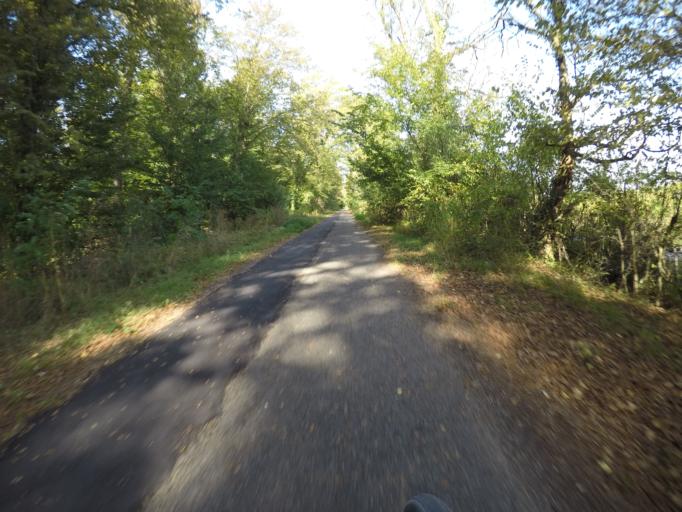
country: DE
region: Baden-Wuerttemberg
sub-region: Karlsruhe Region
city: Kronau
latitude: 49.2048
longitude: 8.6126
